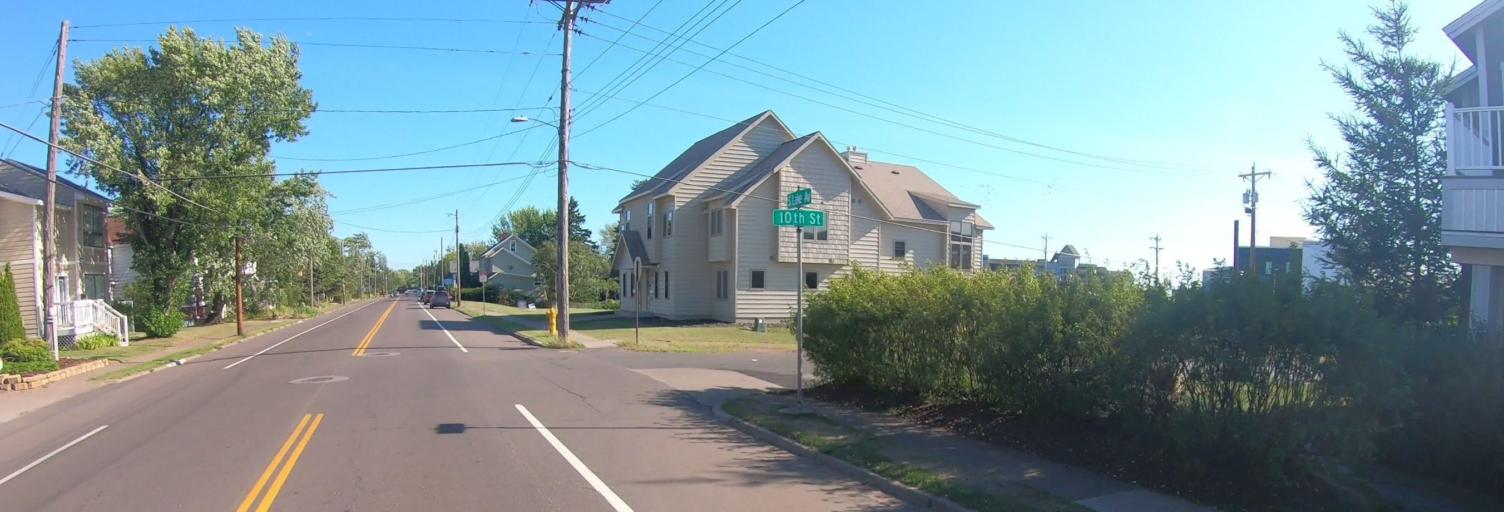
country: US
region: Minnesota
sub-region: Saint Louis County
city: Duluth
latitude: 46.7750
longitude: -92.0902
